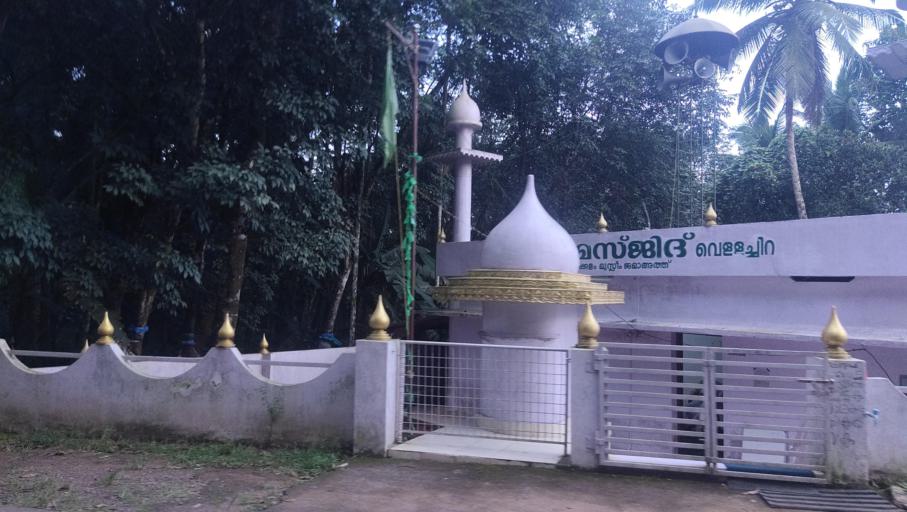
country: IN
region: Kerala
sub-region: Alappuzha
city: Kattanam
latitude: 9.1340
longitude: 76.6372
